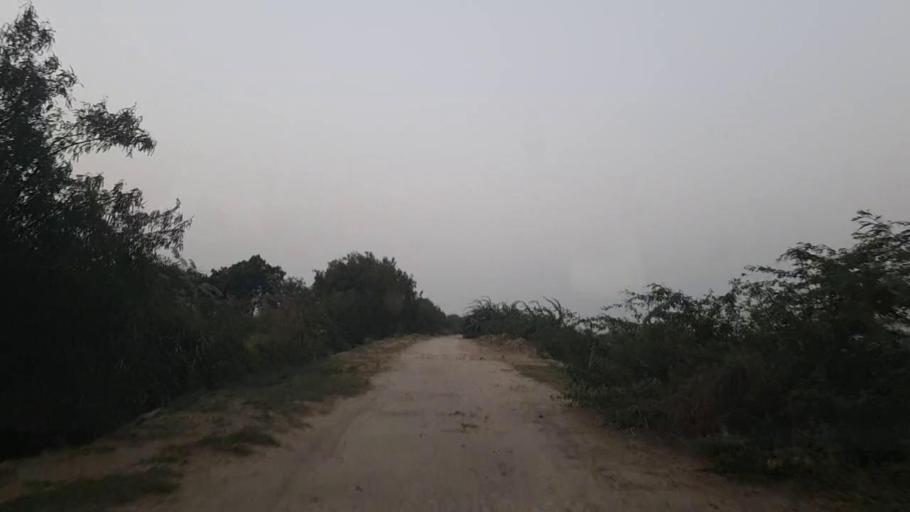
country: PK
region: Sindh
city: Mirpur Sakro
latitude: 24.5801
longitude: 67.7854
